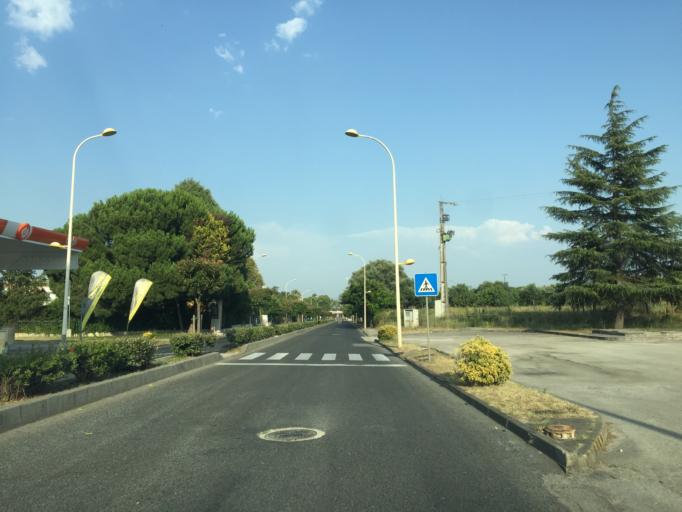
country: PT
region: Santarem
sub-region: Torres Novas
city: Torres Novas
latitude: 39.4733
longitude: -8.5514
